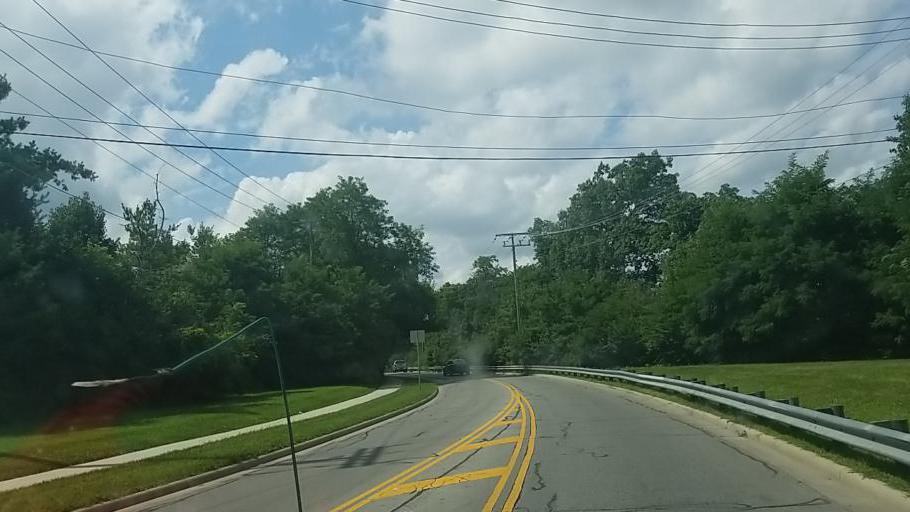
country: US
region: Ohio
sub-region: Franklin County
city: Gahanna
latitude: 40.0450
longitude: -82.8883
